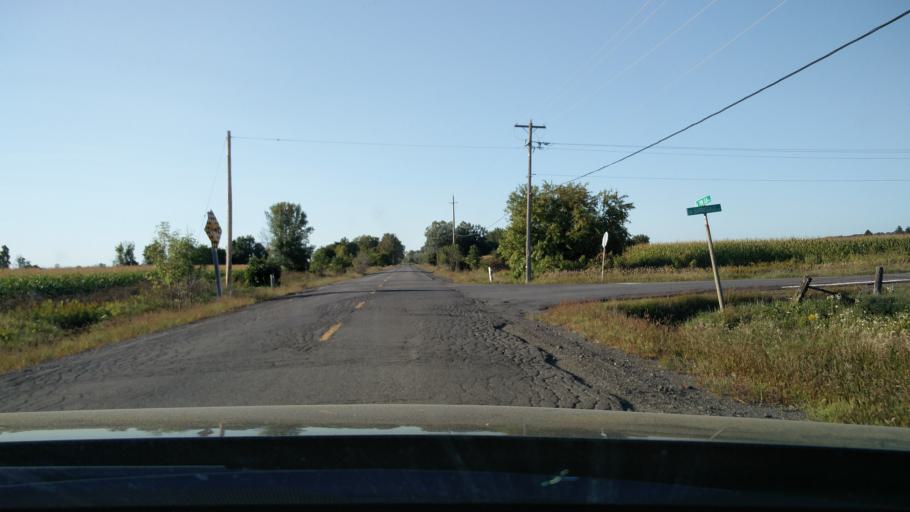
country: CA
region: Ontario
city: Bells Corners
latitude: 45.2080
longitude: -75.7947
